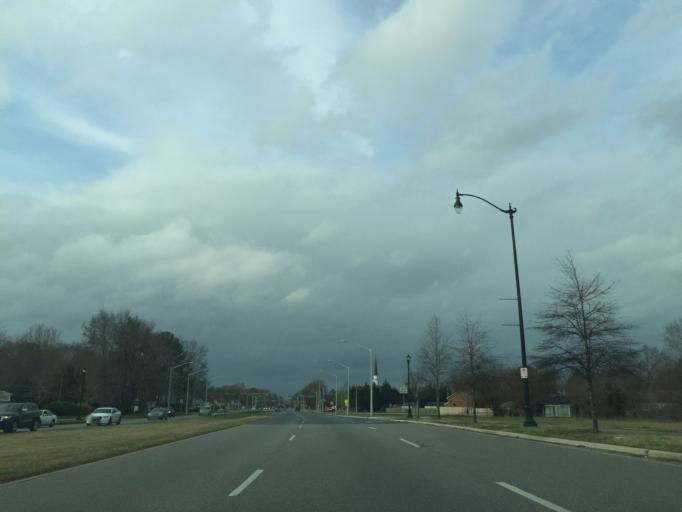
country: US
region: Virginia
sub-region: City of Newport News
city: Newport News
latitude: 37.0856
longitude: -76.4989
